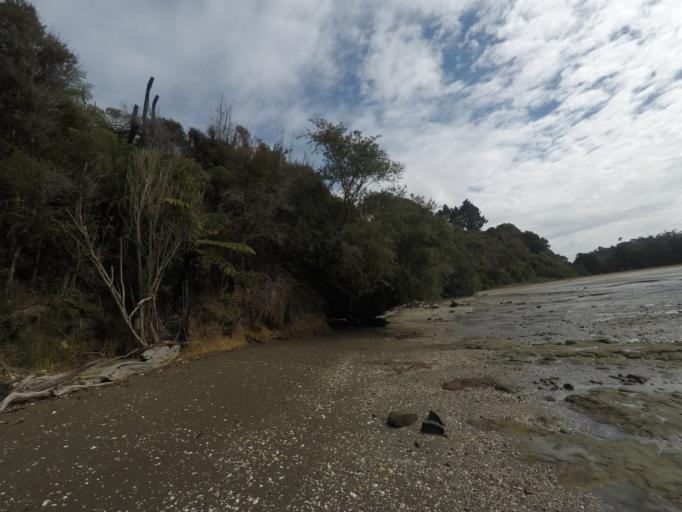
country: NZ
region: Auckland
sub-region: Auckland
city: Rothesay Bay
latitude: -36.6489
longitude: 174.7258
